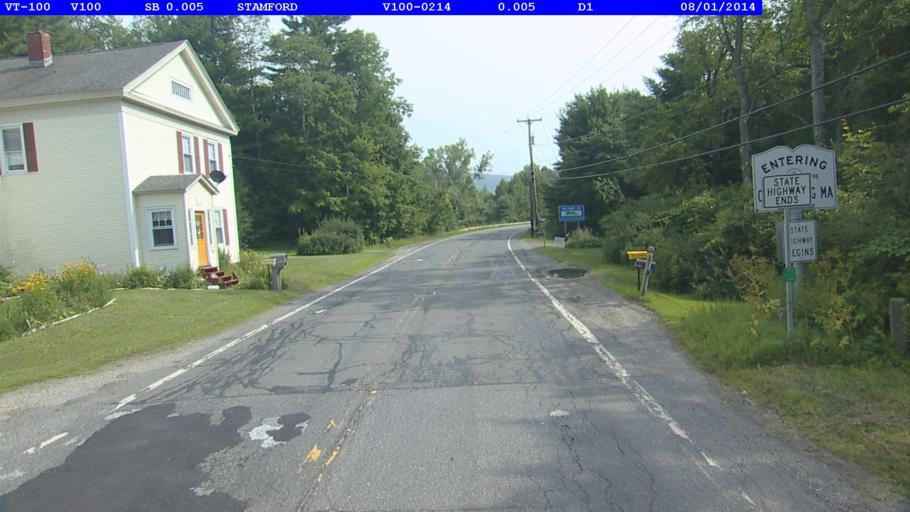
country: US
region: Massachusetts
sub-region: Berkshire County
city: North Adams
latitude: 42.7422
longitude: -73.0715
